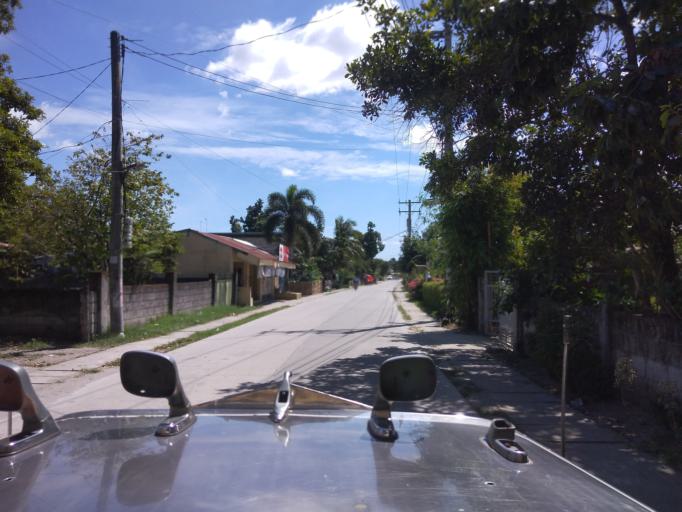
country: PH
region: Central Luzon
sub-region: Province of Pampanga
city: Magliman
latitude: 15.0420
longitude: 120.6446
